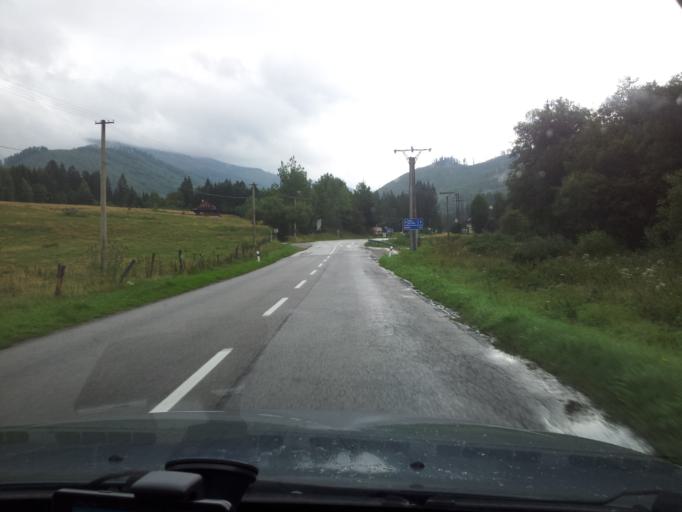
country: SK
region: Banskobystricky
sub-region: Okres Banska Bystrica
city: Brezno
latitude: 48.8642
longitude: 19.6426
